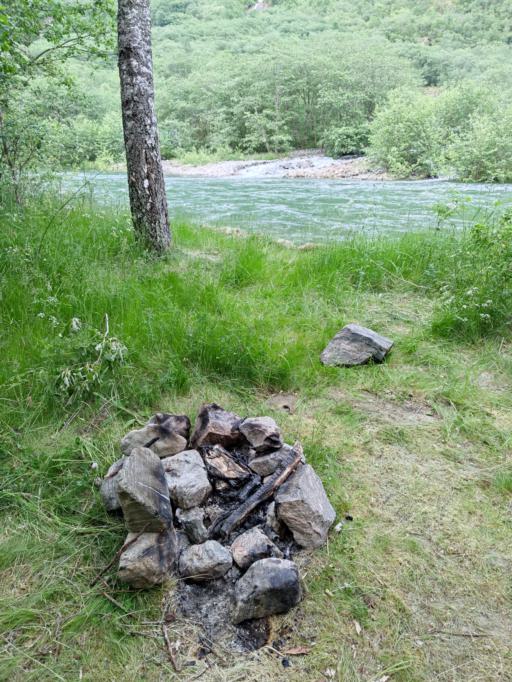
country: NO
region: Sogn og Fjordane
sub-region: Leikanger
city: Hermansverk
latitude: 60.8756
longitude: 6.8376
